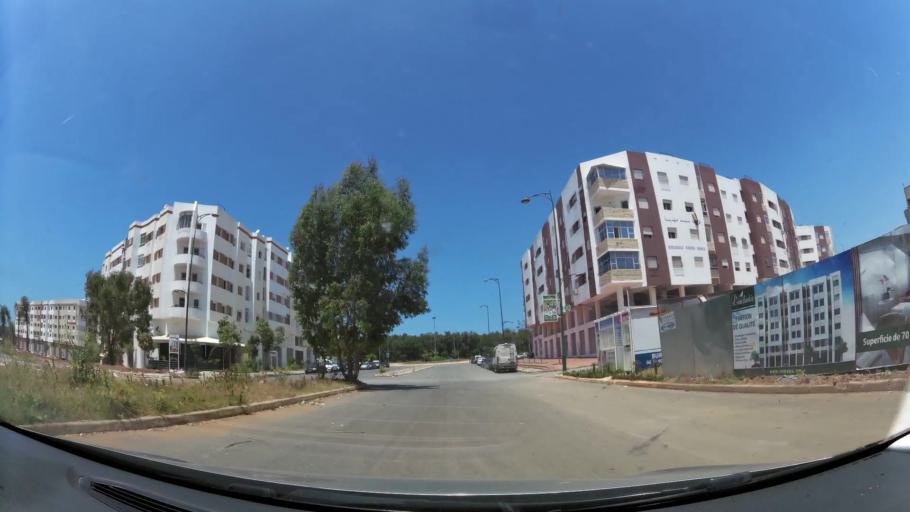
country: MA
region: Gharb-Chrarda-Beni Hssen
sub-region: Kenitra Province
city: Kenitra
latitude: 34.2705
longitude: -6.6279
